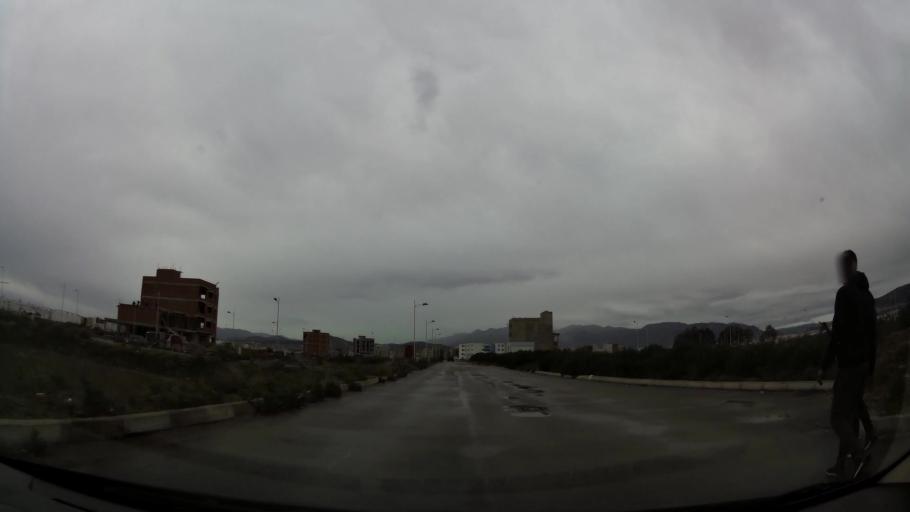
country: MA
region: Tanger-Tetouan
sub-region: Tetouan
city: Martil
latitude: 35.6220
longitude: -5.2993
